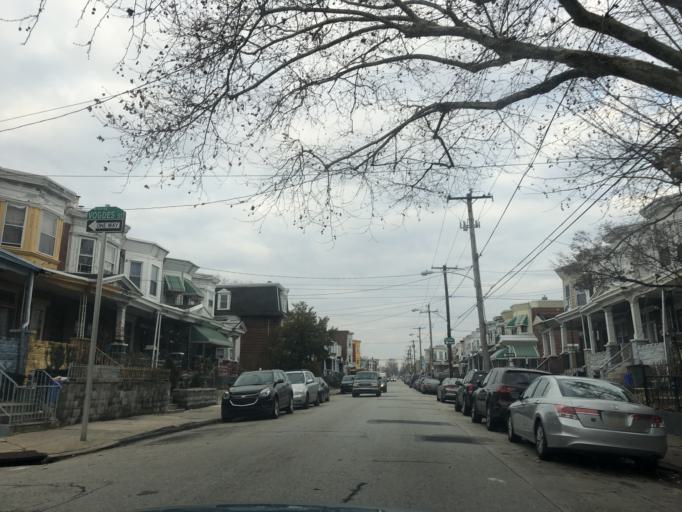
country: US
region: Pennsylvania
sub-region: Delaware County
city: Millbourne
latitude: 39.9753
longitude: -75.2320
